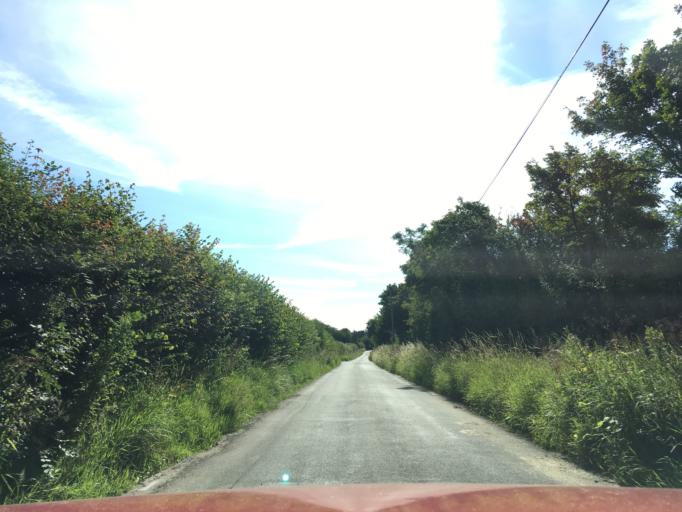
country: GB
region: England
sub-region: South Gloucestershire
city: Bitton
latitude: 51.4401
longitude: -2.4442
